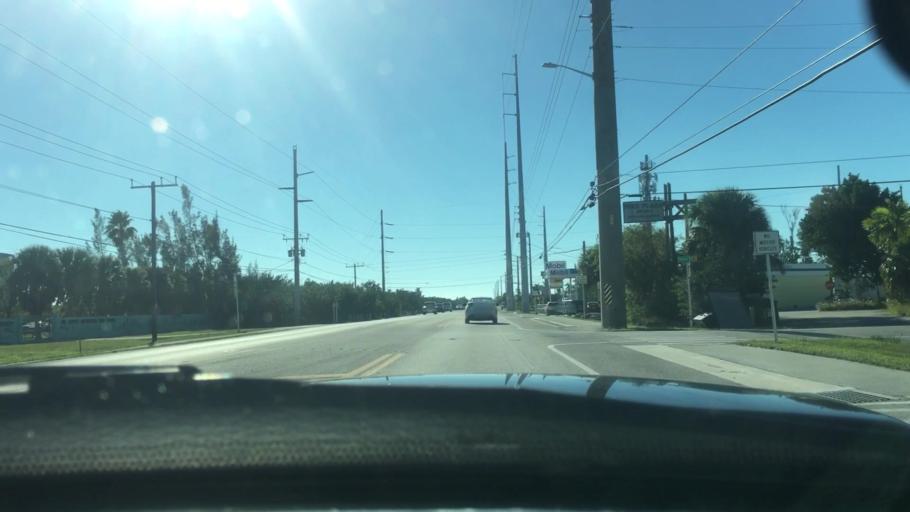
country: US
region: Florida
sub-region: Monroe County
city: Big Coppitt Key
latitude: 24.5966
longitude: -81.6578
